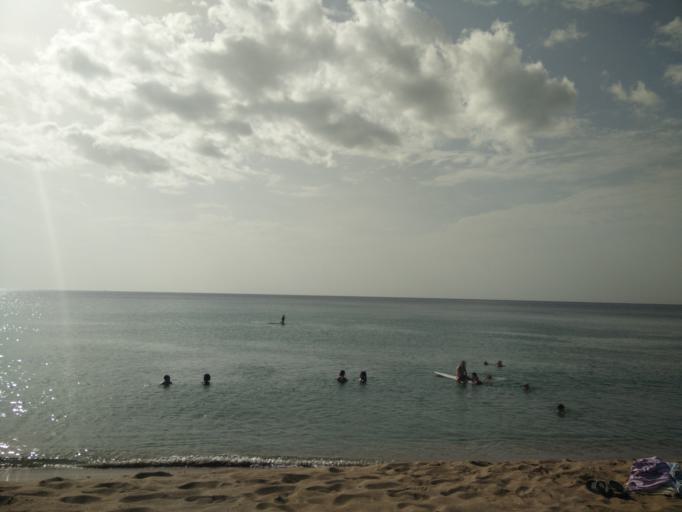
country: GP
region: Guadeloupe
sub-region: Guadeloupe
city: Pointe-Noire
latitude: 16.3214
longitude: -61.7894
